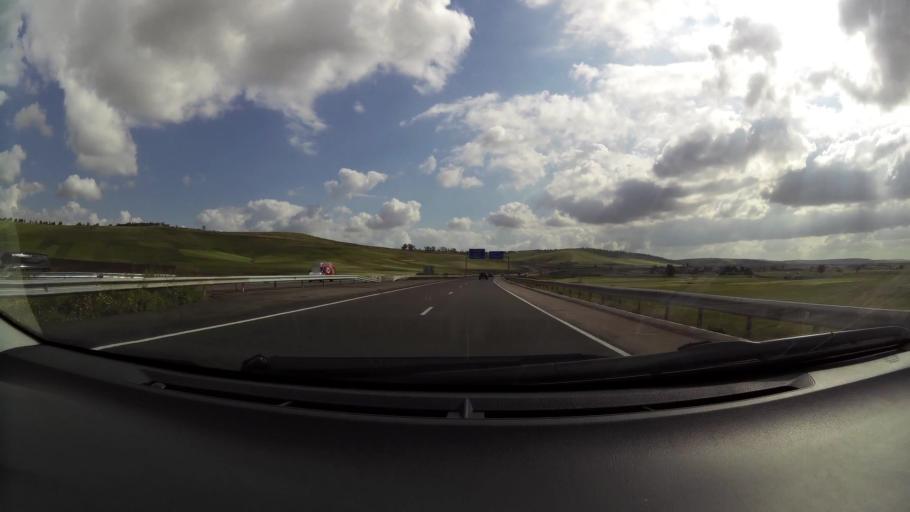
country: MA
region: Chaouia-Ouardigha
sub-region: Settat Province
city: Settat
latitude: 33.0823
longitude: -7.5906
